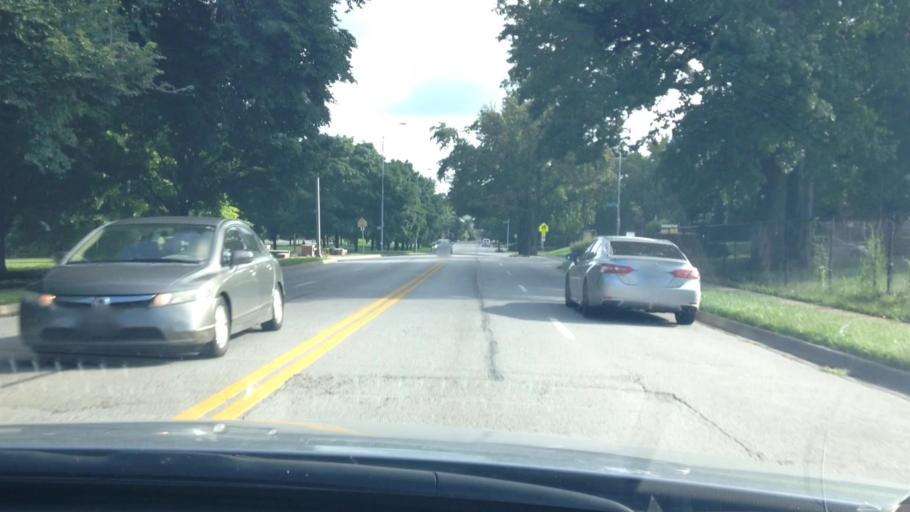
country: US
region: Kansas
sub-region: Johnson County
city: Mission Hills
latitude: 39.0088
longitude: -94.5933
